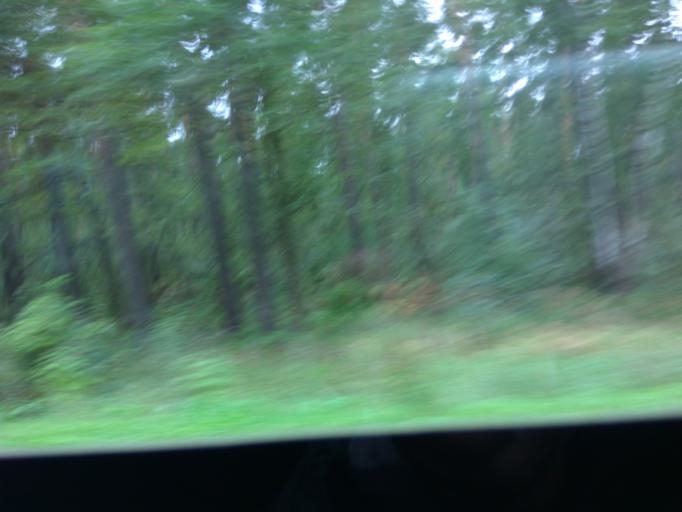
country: RU
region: Moskovskaya
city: Malyshevo
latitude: 55.5231
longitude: 38.3440
